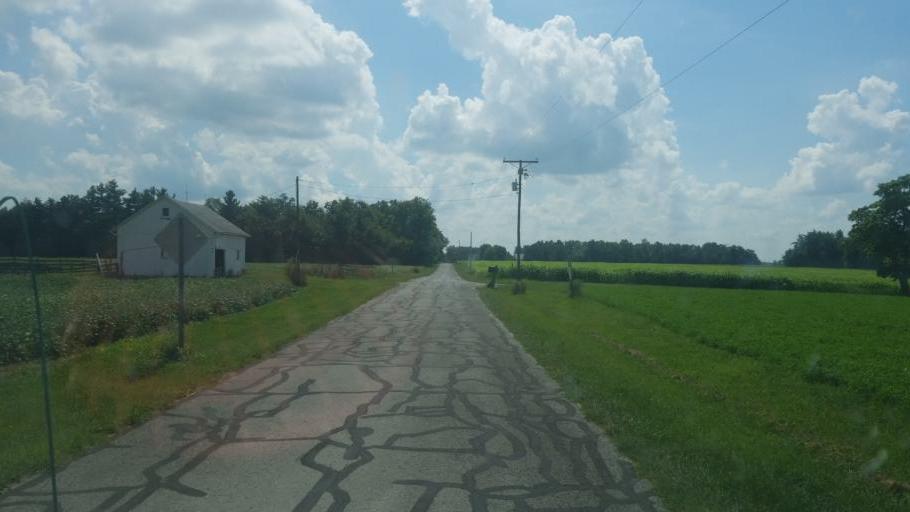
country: US
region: Ohio
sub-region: Hancock County
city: Arlington
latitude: 40.8901
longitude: -83.7080
